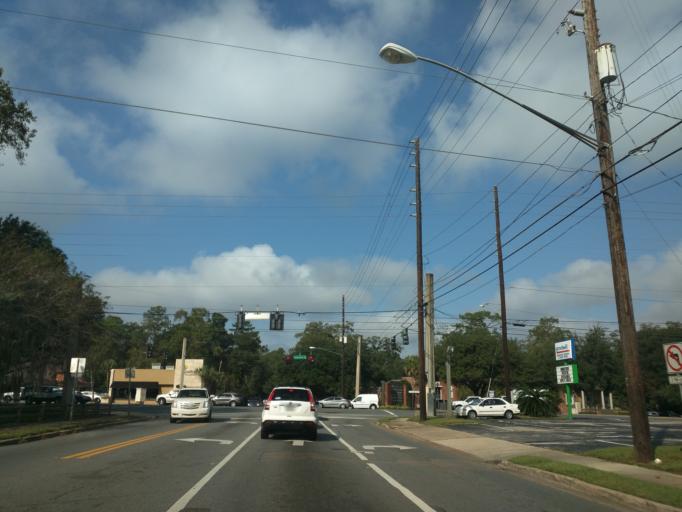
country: US
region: Florida
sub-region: Leon County
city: Tallahassee
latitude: 30.4664
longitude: -84.2678
